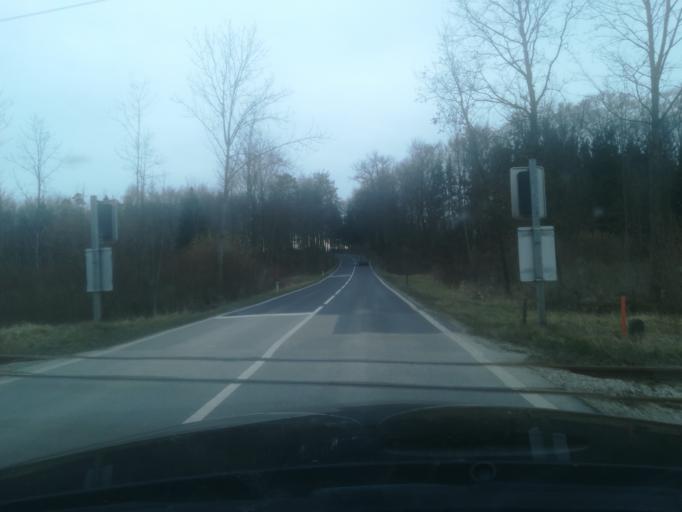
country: AT
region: Upper Austria
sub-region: Wels-Land
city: Lambach
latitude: 48.0798
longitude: 13.8833
